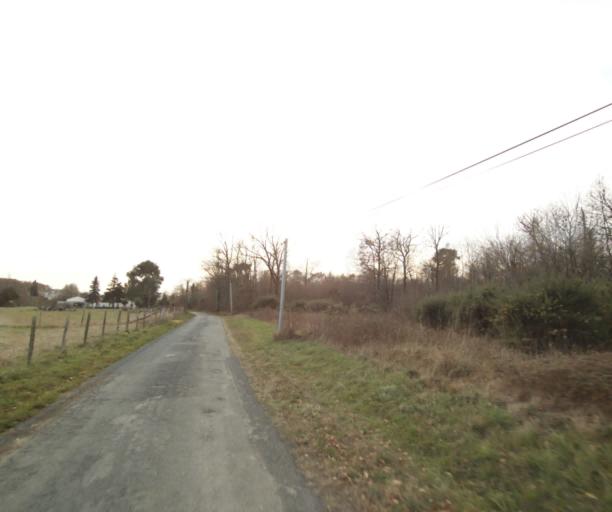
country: FR
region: Poitou-Charentes
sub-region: Departement de la Charente-Maritime
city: Fontcouverte
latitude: 45.7855
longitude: -0.5830
